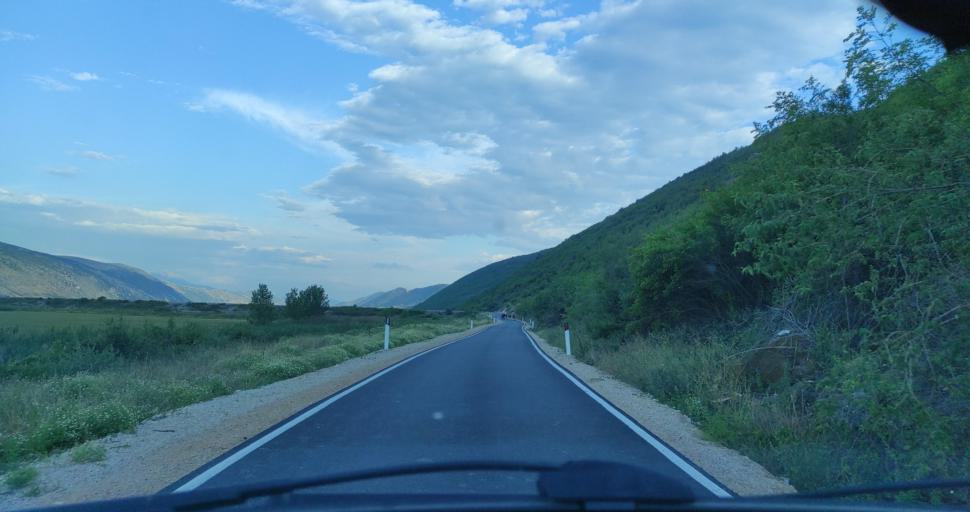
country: AL
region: Shkoder
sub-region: Rrethi i Shkodres
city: Velipoje
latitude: 41.9246
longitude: 19.4504
